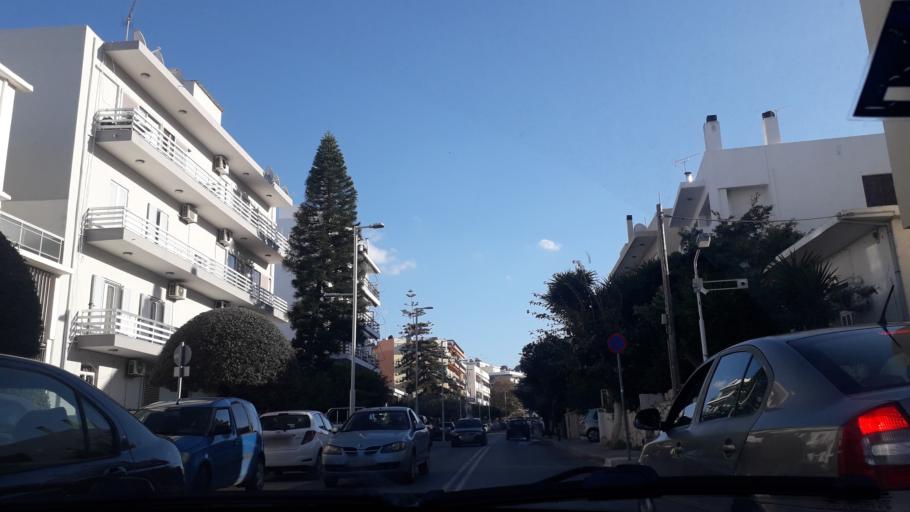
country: GR
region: Crete
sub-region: Nomos Rethymnis
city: Rethymno
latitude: 35.3647
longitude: 24.4709
